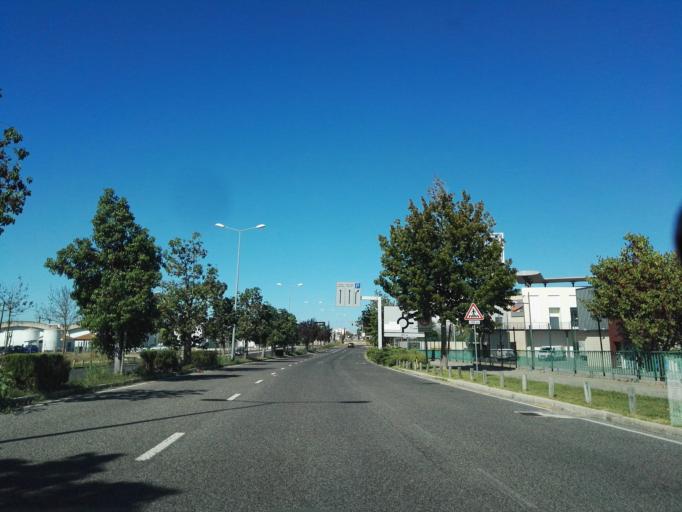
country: PT
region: Setubal
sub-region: Alcochete
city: Alcochete
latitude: 38.7507
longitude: -8.9413
